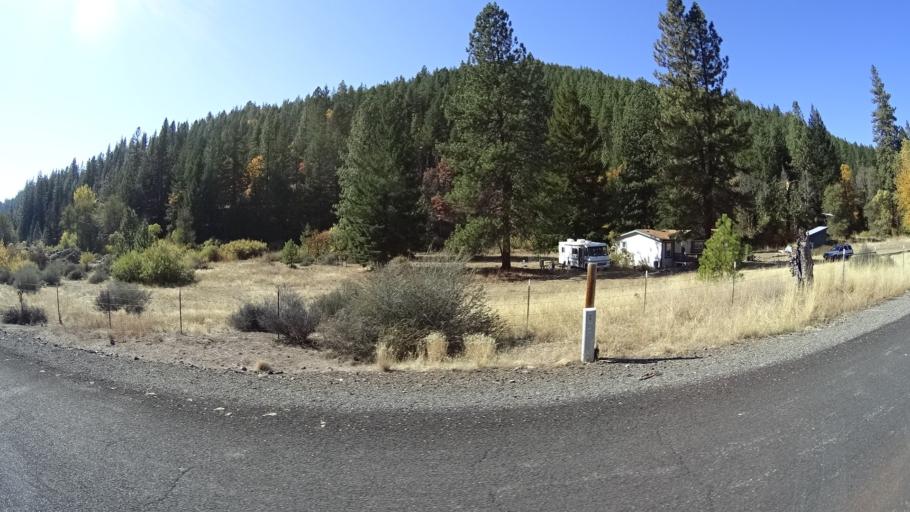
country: US
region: California
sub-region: Siskiyou County
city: Yreka
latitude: 41.6831
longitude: -122.8513
